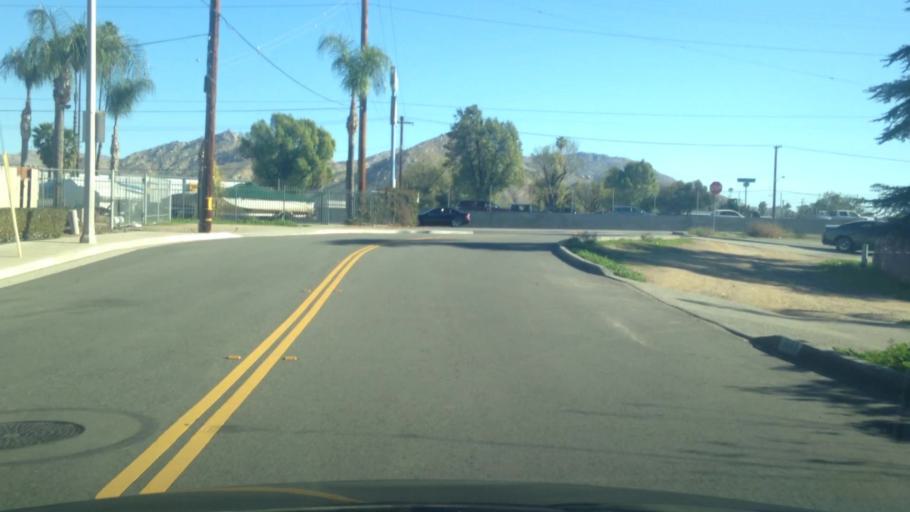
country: US
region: California
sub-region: Riverside County
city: Highgrove
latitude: 34.0081
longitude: -117.3487
